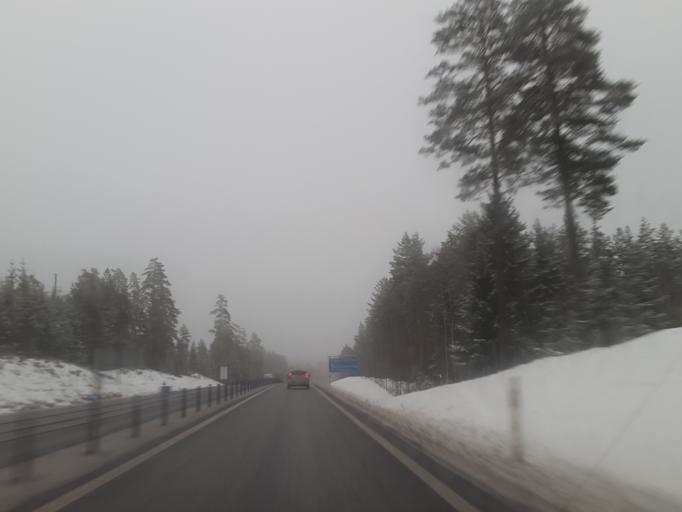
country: SE
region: Joenkoeping
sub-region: Mullsjo Kommun
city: Mullsjoe
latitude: 57.7542
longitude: 13.8878
